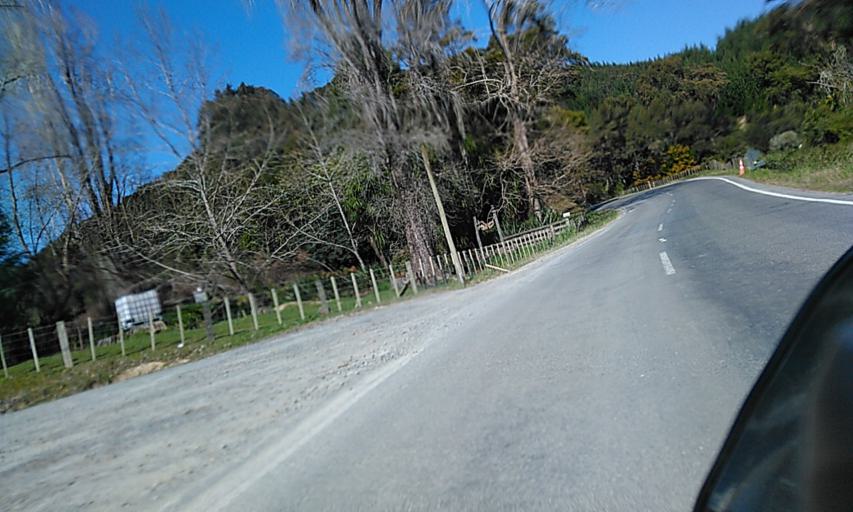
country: NZ
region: Gisborne
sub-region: Gisborne District
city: Gisborne
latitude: -38.3272
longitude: 178.1748
